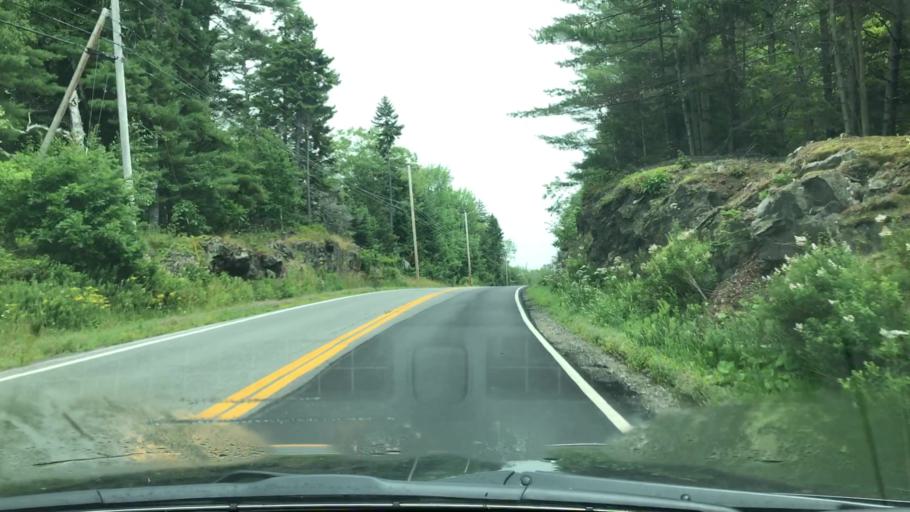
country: US
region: Maine
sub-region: Waldo County
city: Lincolnville
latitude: 44.3019
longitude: -68.9890
